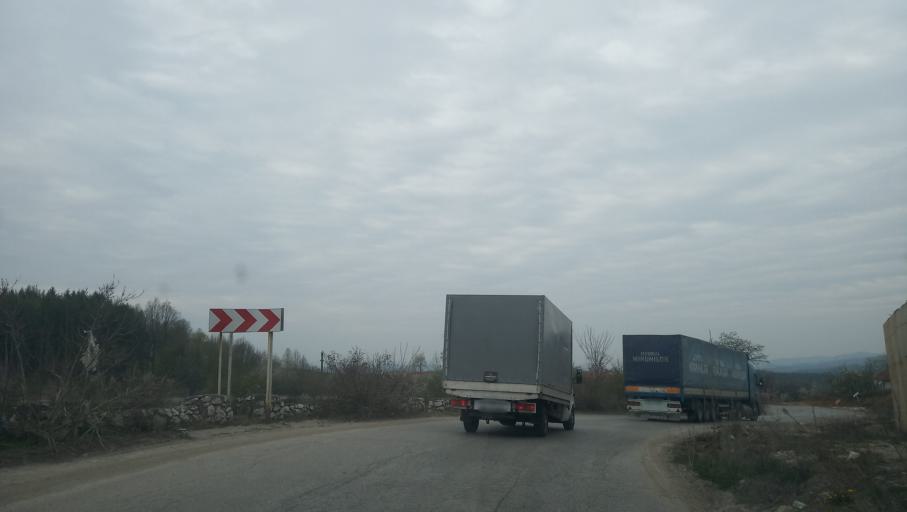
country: RO
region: Arad
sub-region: Comuna Varfurile
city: Varfurile
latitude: 46.3676
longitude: 22.5510
